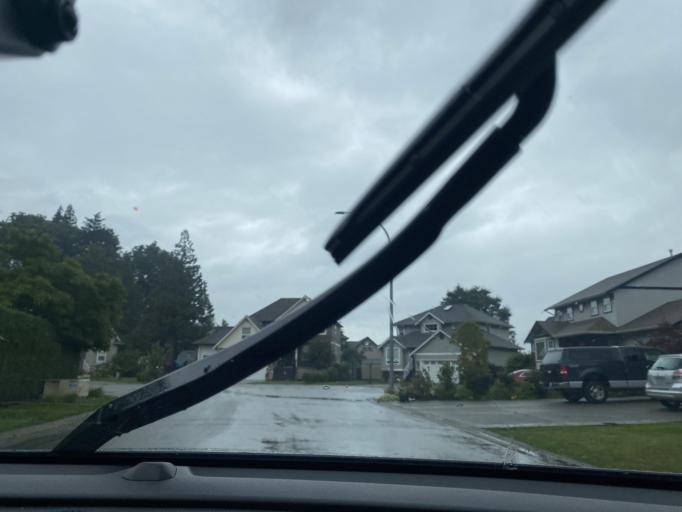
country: CA
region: British Columbia
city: Agassiz
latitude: 49.2966
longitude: -121.7814
